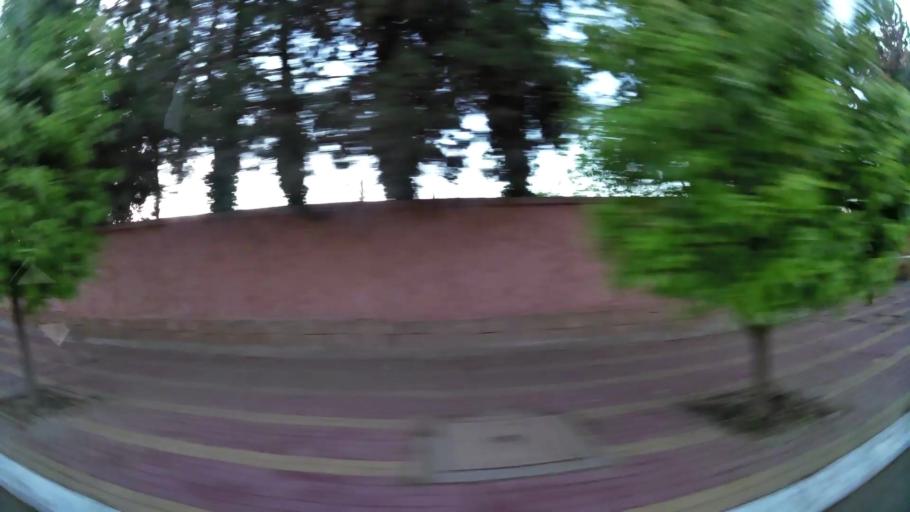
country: MA
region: Marrakech-Tensift-Al Haouz
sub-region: Kelaa-Des-Sraghna
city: Sidi Bou Othmane
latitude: 32.2102
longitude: -7.9326
